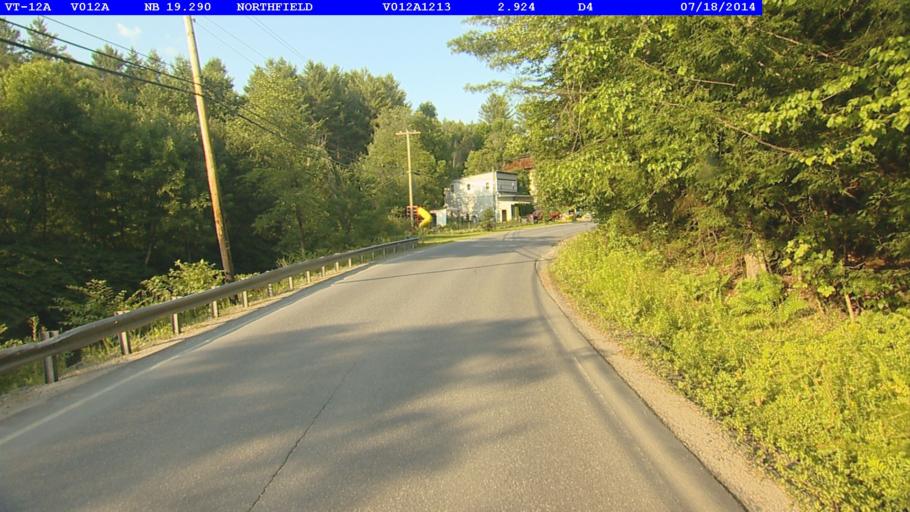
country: US
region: Vermont
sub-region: Washington County
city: Northfield
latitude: 44.1171
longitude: -72.6747
